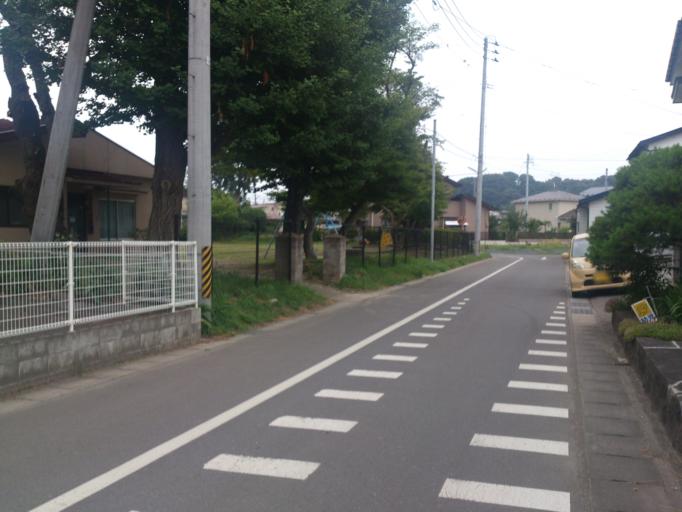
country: JP
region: Iwate
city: Ichinoseki
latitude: 38.9288
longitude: 141.1200
